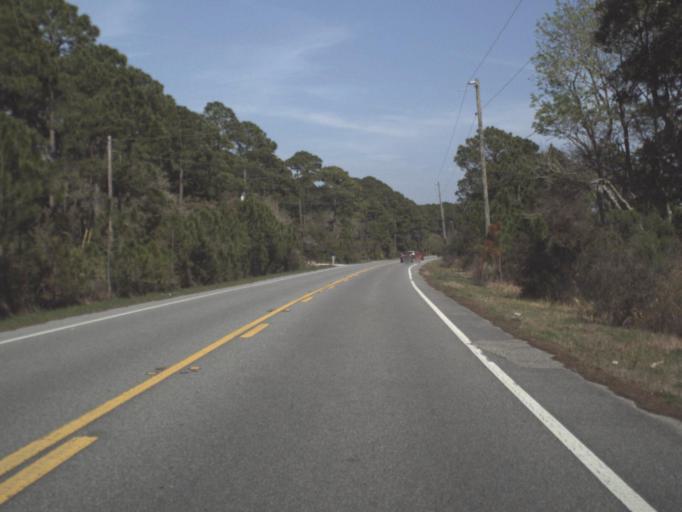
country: US
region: Florida
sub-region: Franklin County
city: Eastpoint
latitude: 29.7671
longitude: -84.8067
